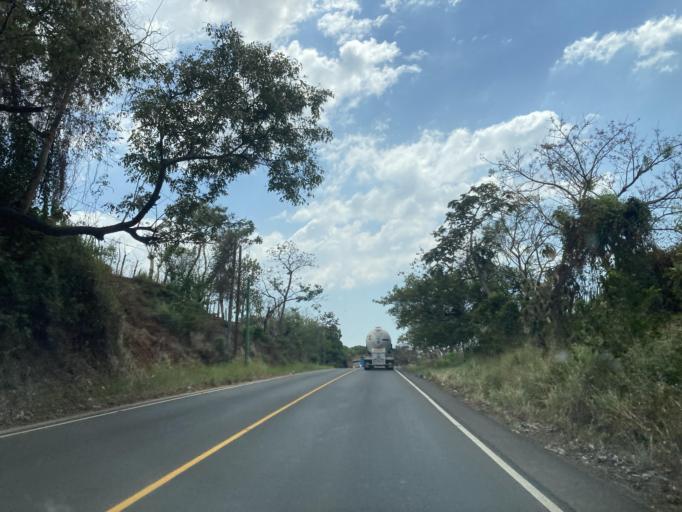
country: GT
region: Santa Rosa
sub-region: Municipio de Taxisco
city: Taxisco
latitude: 14.0826
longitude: -90.4902
